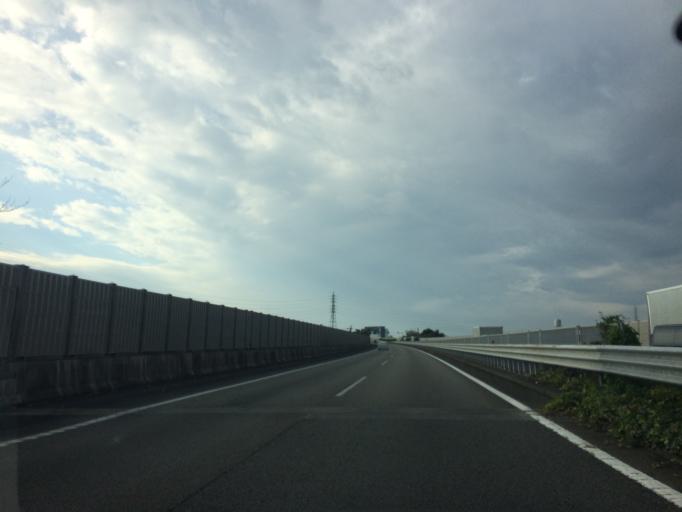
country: JP
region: Shizuoka
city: Shizuoka-shi
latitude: 35.0082
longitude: 138.4338
